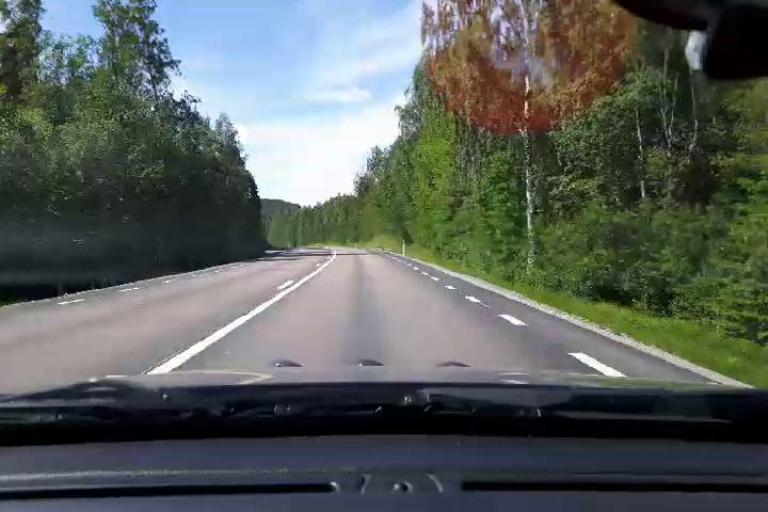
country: SE
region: Gaevleborg
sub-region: Bollnas Kommun
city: Kilafors
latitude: 61.1846
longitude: 16.7809
